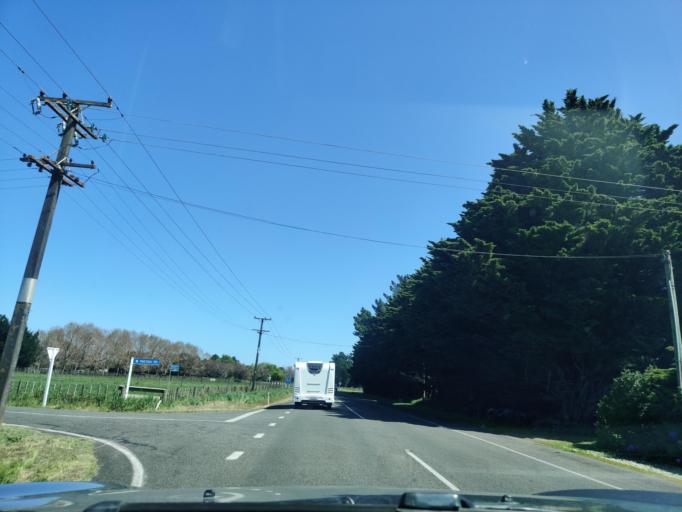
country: NZ
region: Taranaki
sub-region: South Taranaki District
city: Patea
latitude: -39.8089
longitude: 174.7681
